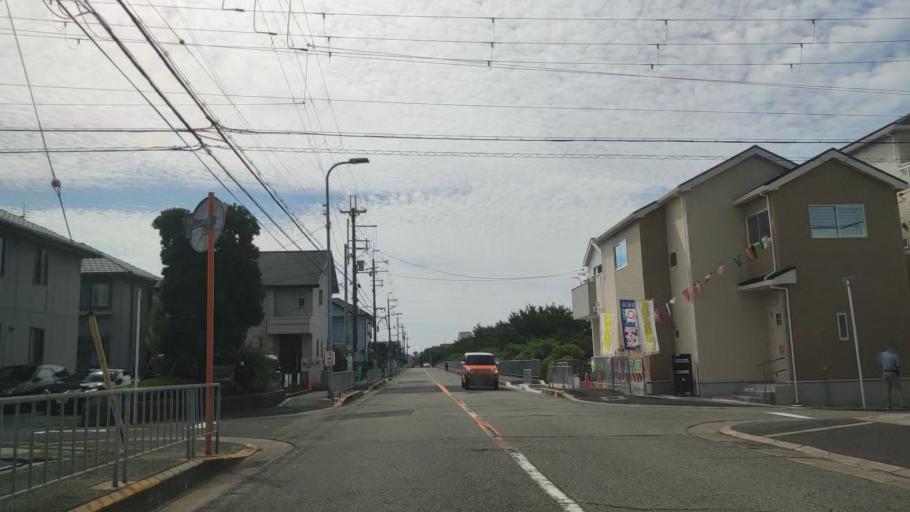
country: JP
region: Osaka
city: Ikeda
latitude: 34.8137
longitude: 135.4351
